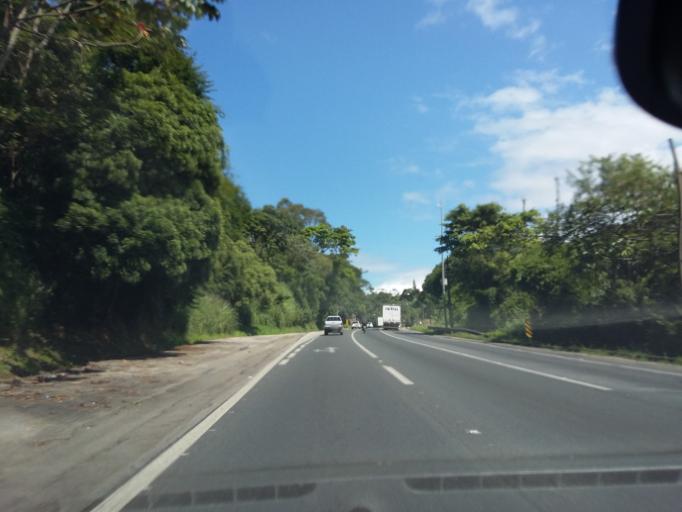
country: BR
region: Santa Catarina
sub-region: Itapema
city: Itapema
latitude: -27.0397
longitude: -48.5999
